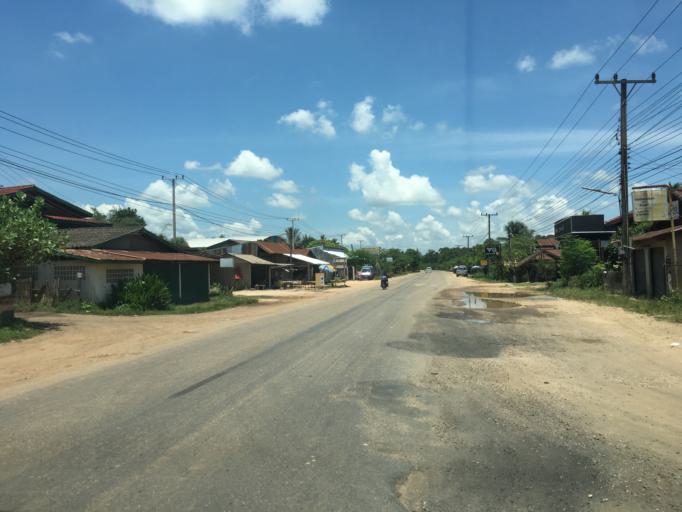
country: LA
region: Vientiane
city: Vientiane
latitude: 18.2154
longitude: 102.4984
